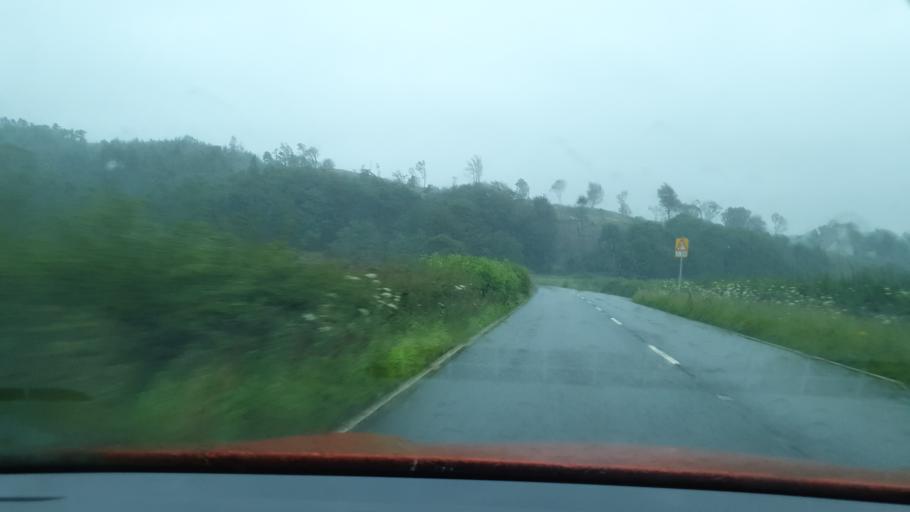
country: GB
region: England
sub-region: Cumbria
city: Askam in Furness
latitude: 54.2665
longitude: -3.1837
